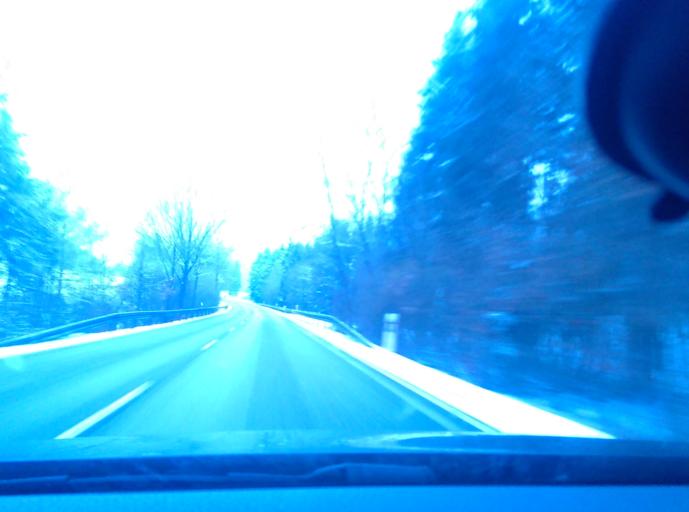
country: DE
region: Thuringia
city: Gerstungen
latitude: 51.0202
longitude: 10.0376
